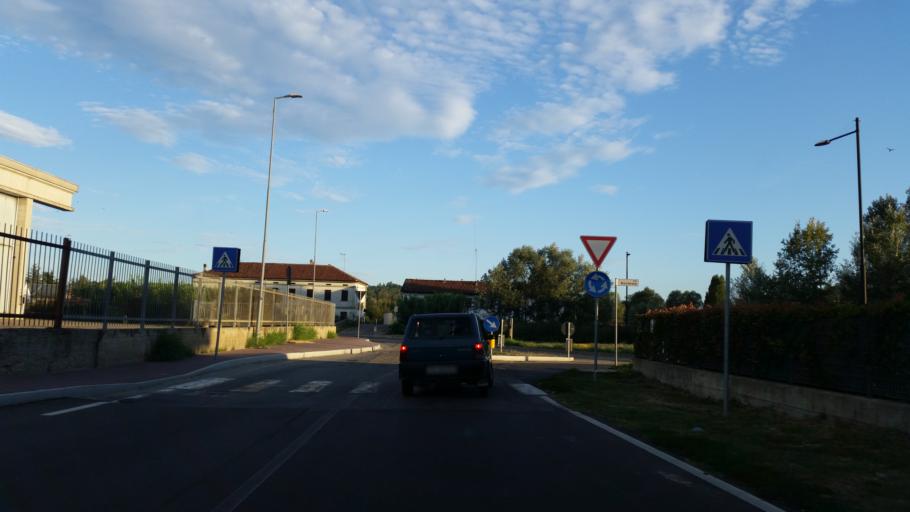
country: IT
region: Piedmont
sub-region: Provincia di Asti
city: Asti
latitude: 44.8895
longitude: 8.2065
